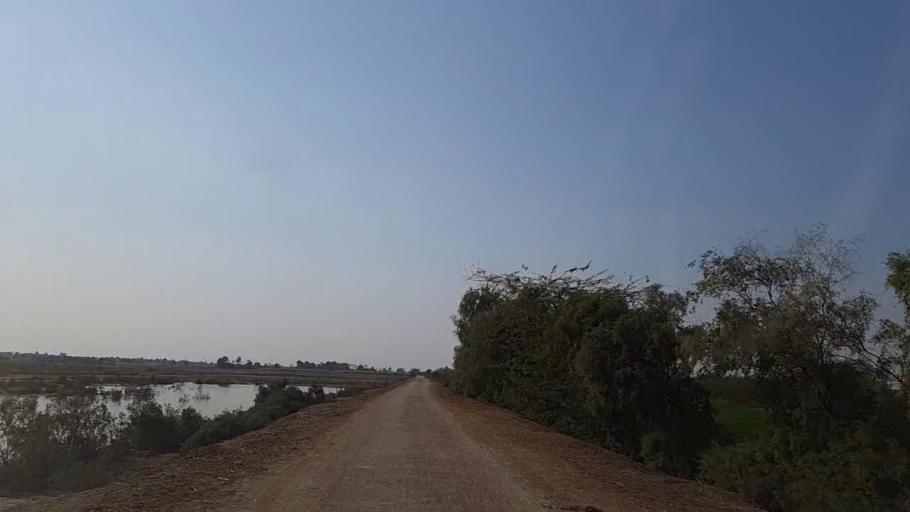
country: PK
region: Sindh
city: Daur
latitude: 26.4367
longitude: 68.2666
